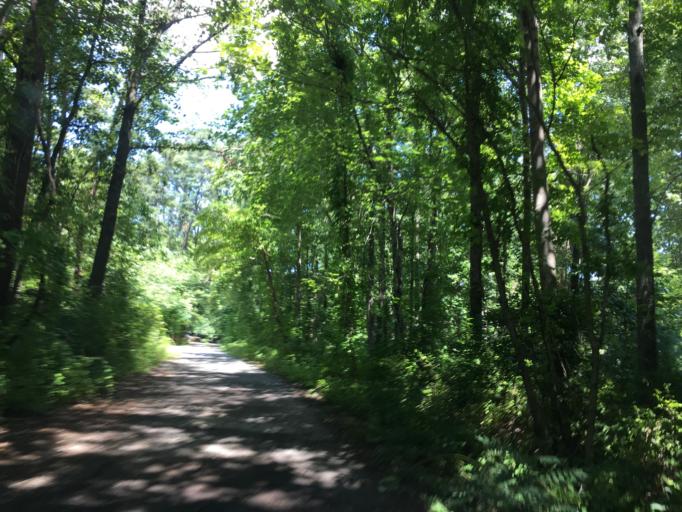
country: US
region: Maryland
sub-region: Anne Arundel County
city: Pasadena
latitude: 39.0893
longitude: -76.5595
